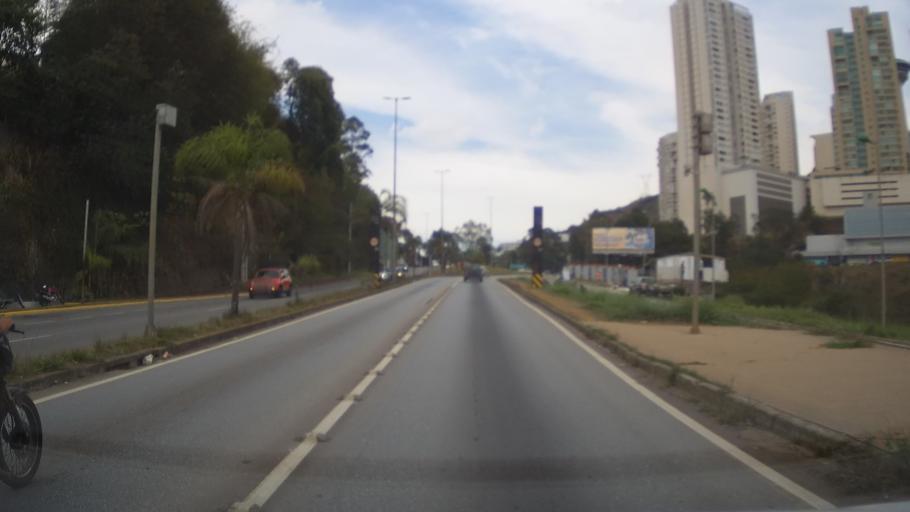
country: BR
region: Minas Gerais
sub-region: Belo Horizonte
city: Belo Horizonte
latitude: -19.9873
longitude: -43.9418
